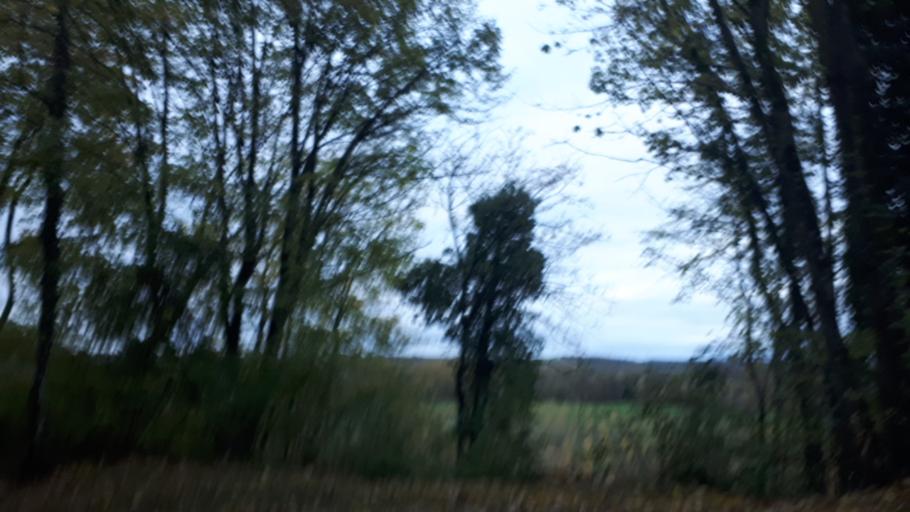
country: FR
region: Centre
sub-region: Departement du Loir-et-Cher
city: Lunay
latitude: 47.7654
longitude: 0.9367
